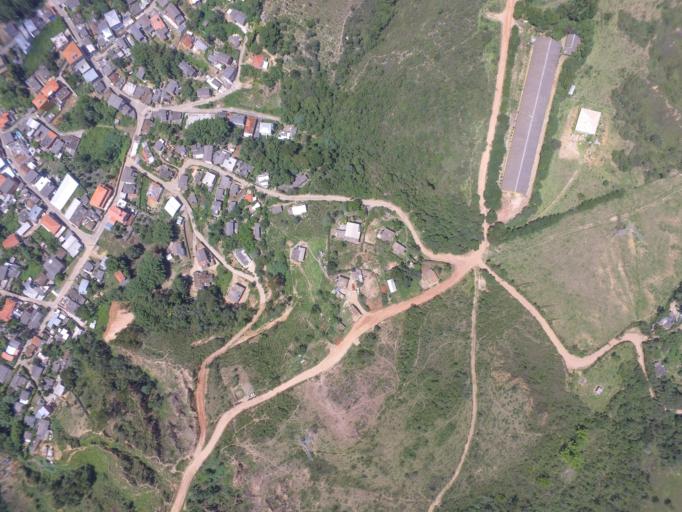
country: BR
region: Minas Gerais
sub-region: Tiradentes
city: Tiradentes
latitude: -21.0507
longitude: -44.0759
